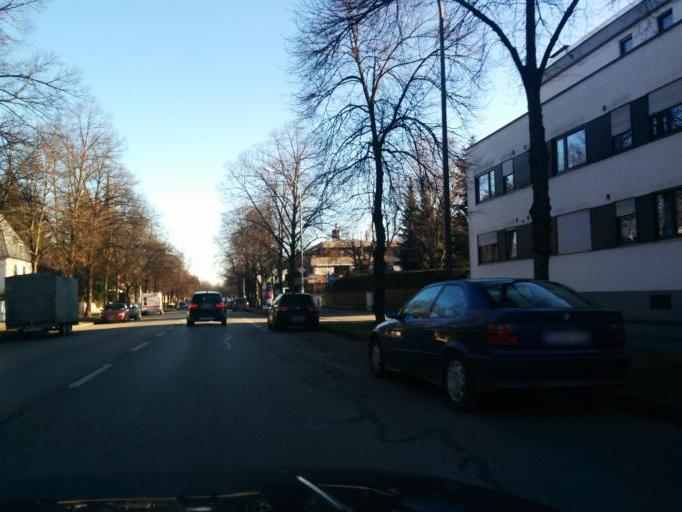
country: DE
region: Bavaria
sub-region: Upper Bavaria
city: Munich
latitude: 48.0906
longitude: 11.5644
